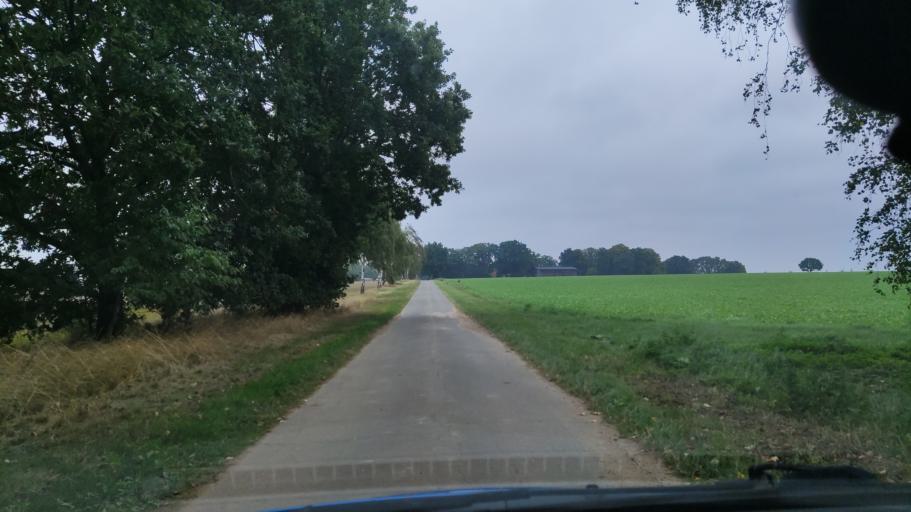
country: DE
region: Lower Saxony
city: Altenmedingen
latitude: 53.1267
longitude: 10.6213
